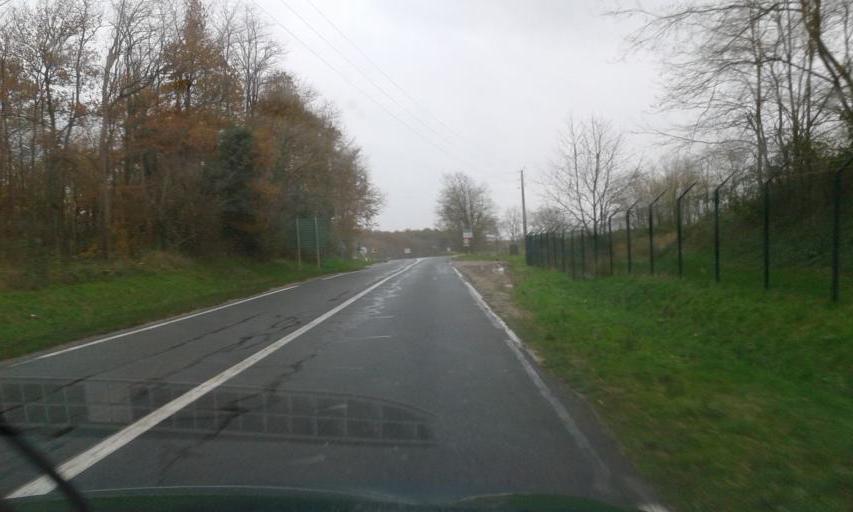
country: FR
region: Centre
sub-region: Departement du Loiret
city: Fay-aux-Loges
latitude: 47.9074
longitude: 2.1320
